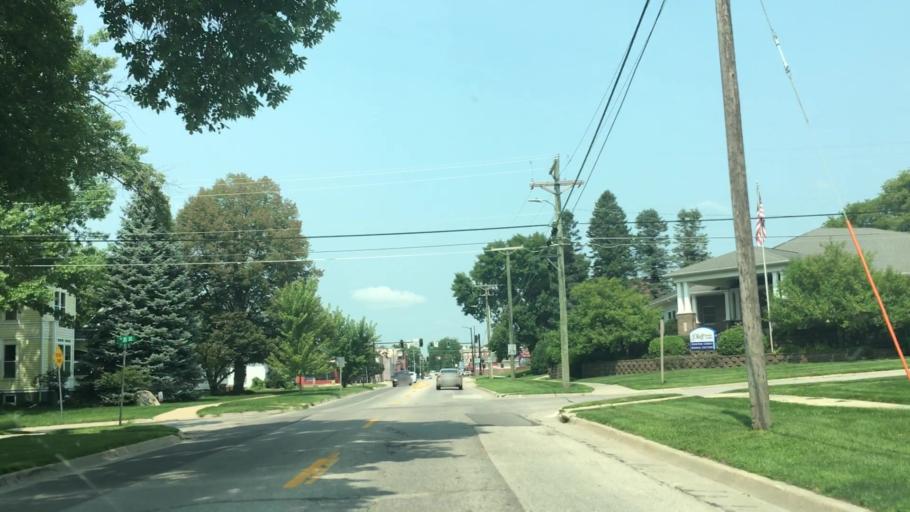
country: US
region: Iowa
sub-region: Buchanan County
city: Independence
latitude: 42.4663
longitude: -91.8917
